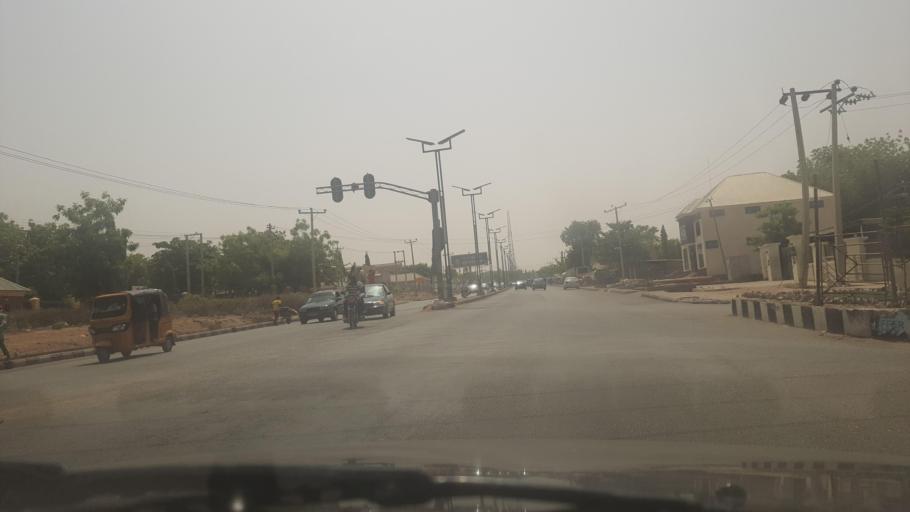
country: NG
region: Gombe
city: Gombe
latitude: 10.2861
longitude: 11.1405
